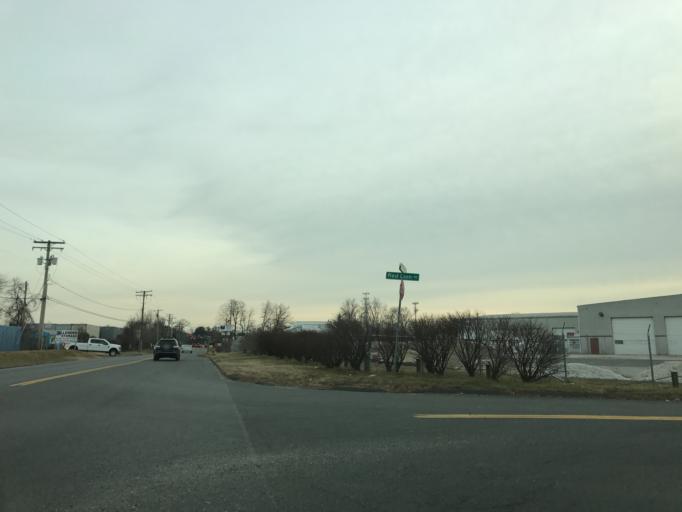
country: US
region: Maryland
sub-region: Baltimore County
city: White Marsh
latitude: 39.4004
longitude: -76.4068
